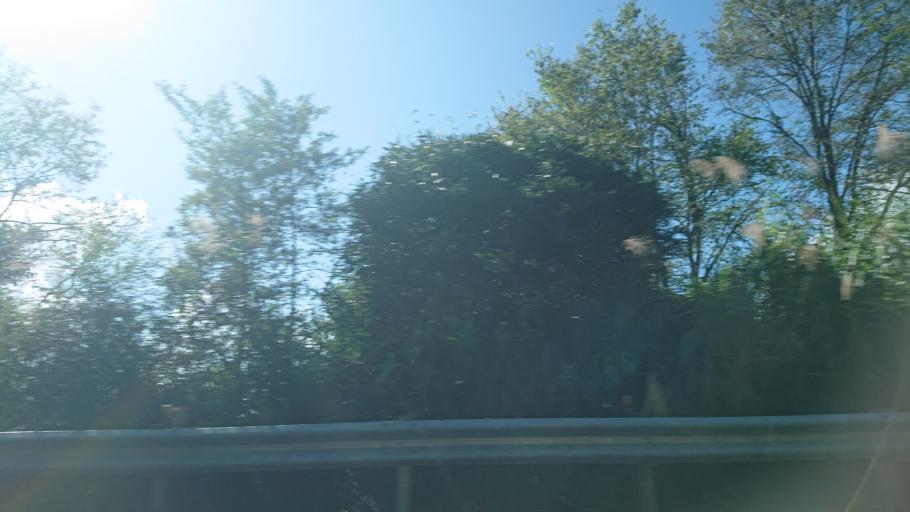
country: TW
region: Taiwan
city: Lugu
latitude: 23.4873
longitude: 120.8225
